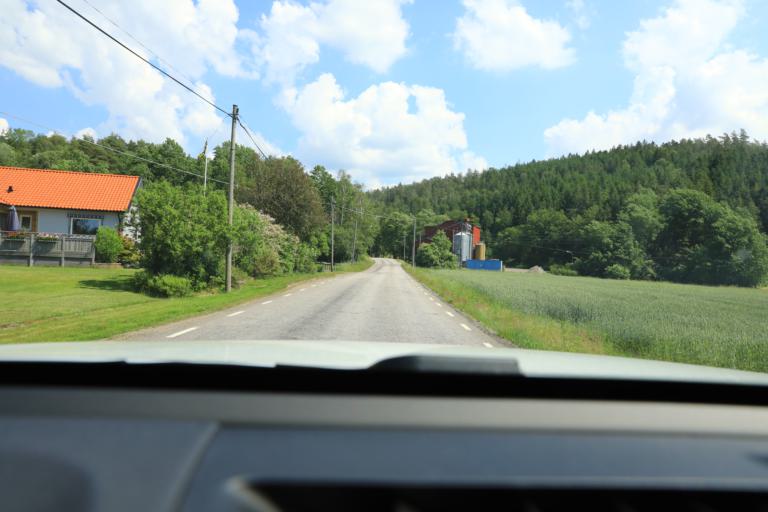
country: SE
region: Halland
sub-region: Varbergs Kommun
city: Veddige
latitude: 57.2038
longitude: 12.3306
